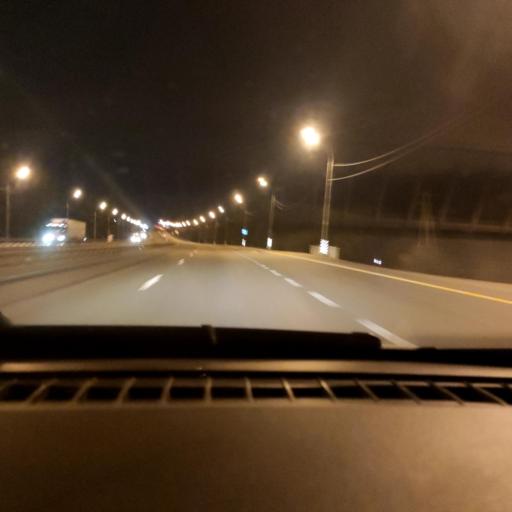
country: RU
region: Lipetsk
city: Khlevnoye
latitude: 52.0946
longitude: 39.1766
